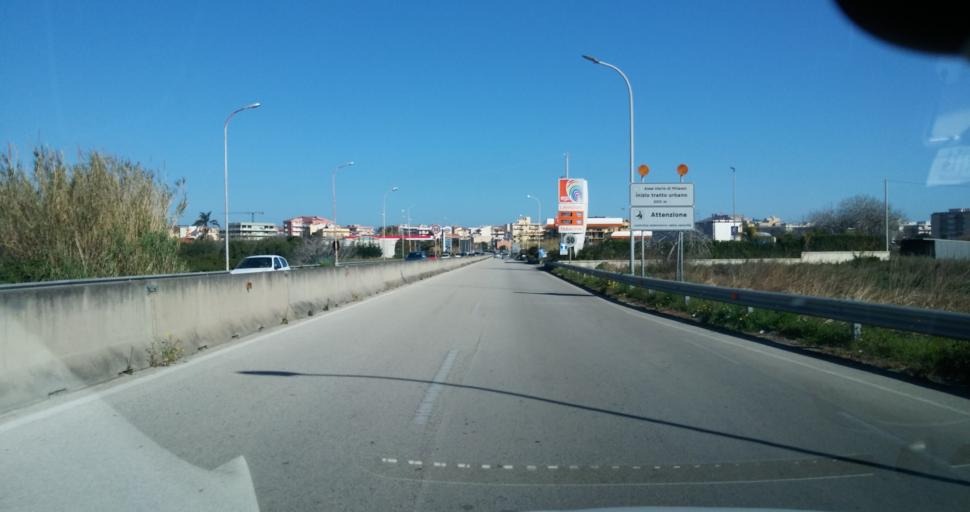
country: IT
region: Sicily
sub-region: Messina
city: Milazzo
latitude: 38.2098
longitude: 15.2376
